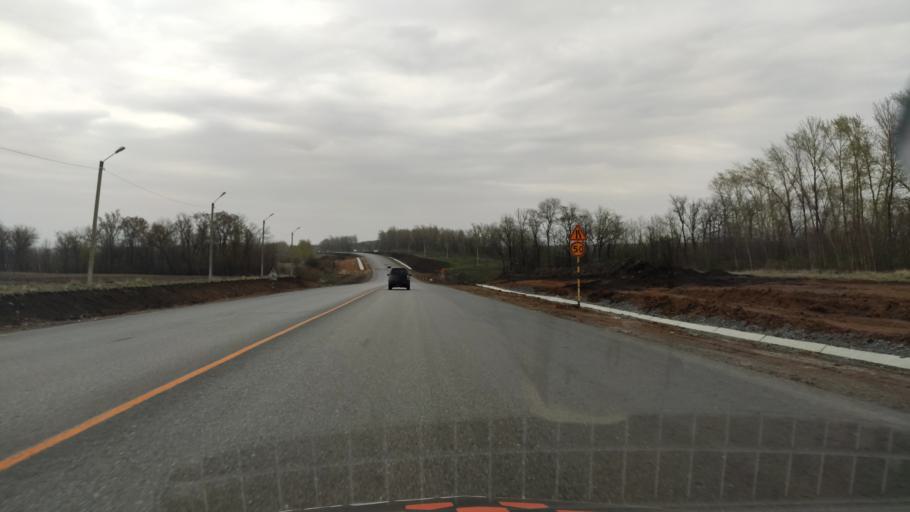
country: RU
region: Kursk
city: Gorshechnoye
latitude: 51.5498
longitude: 38.0468
